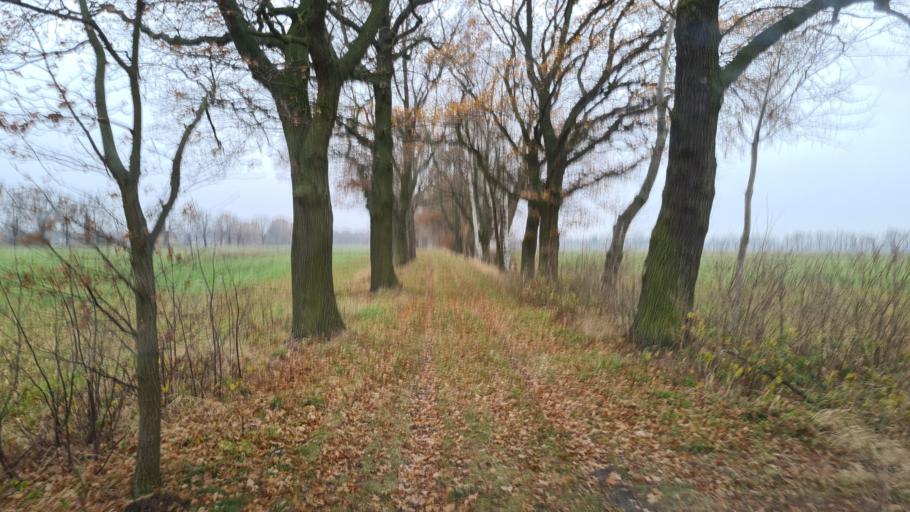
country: DE
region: Brandenburg
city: Schraden
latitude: 51.4161
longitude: 13.7123
